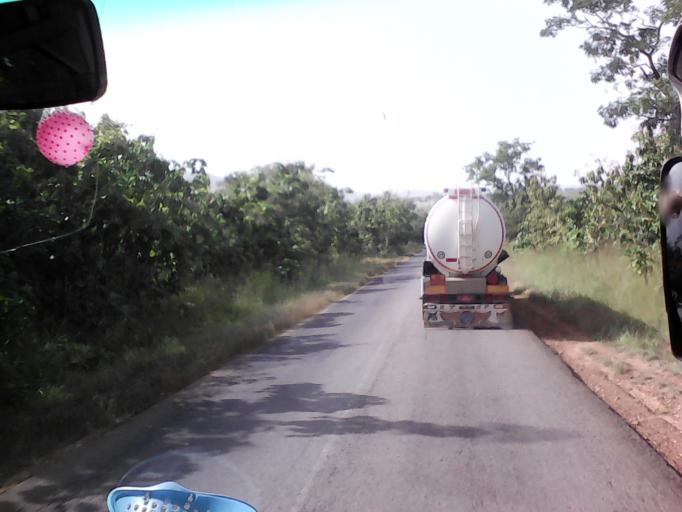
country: TG
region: Centrale
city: Sokode
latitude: 9.0811
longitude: 1.1354
